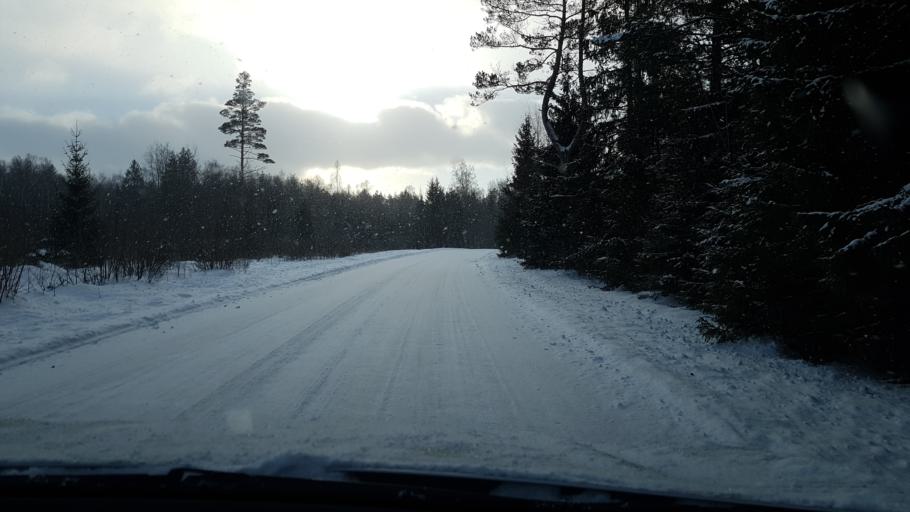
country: EE
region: Harju
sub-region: Nissi vald
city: Turba
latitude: 59.1842
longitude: 24.1409
